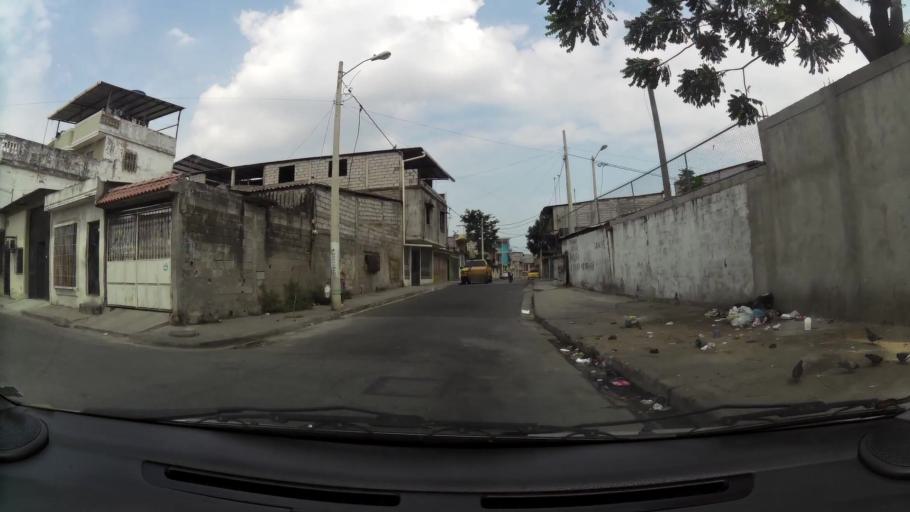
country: EC
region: Guayas
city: Guayaquil
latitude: -2.2332
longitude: -79.9062
